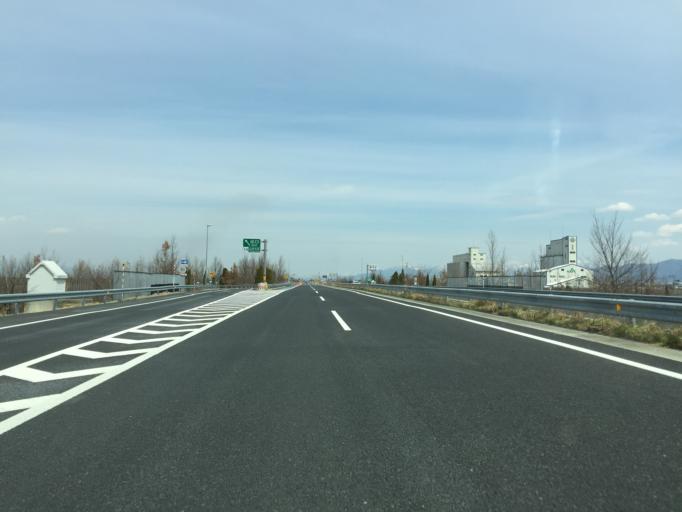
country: JP
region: Yamagata
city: Yamagata-shi
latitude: 38.2696
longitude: 140.2926
